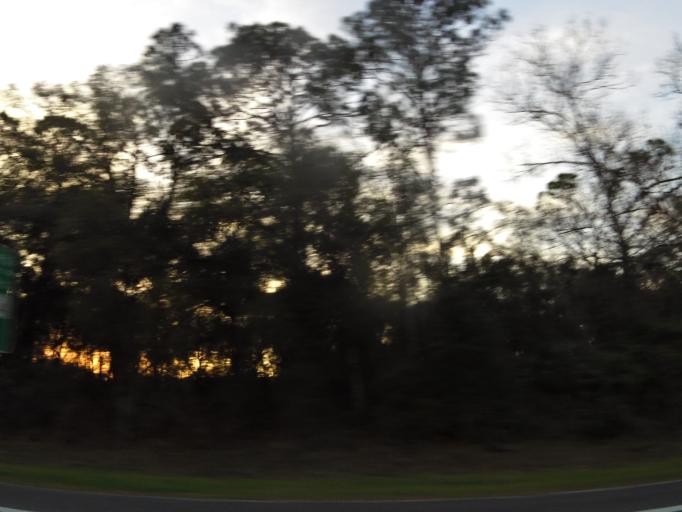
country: US
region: Florida
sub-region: Volusia County
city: North DeLand
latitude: 29.1086
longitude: -81.2943
